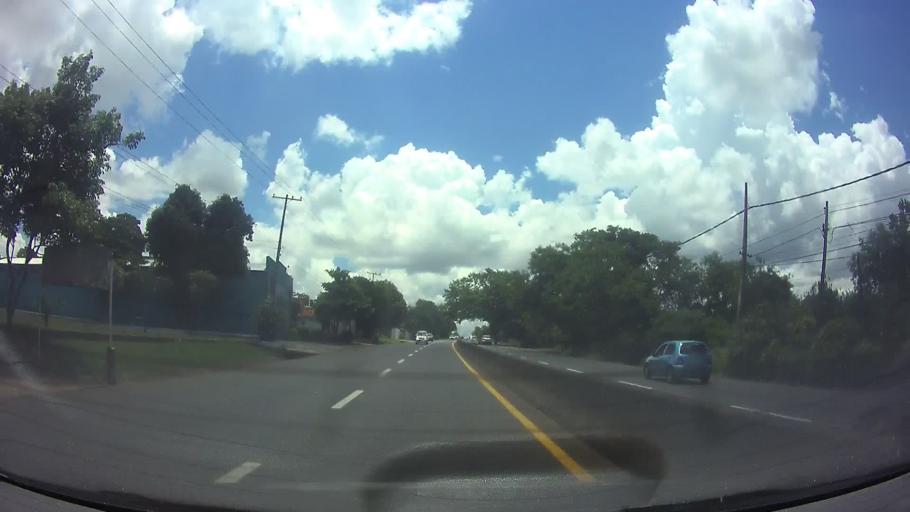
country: PY
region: Central
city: Itaugua
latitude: -25.3847
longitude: -57.3704
